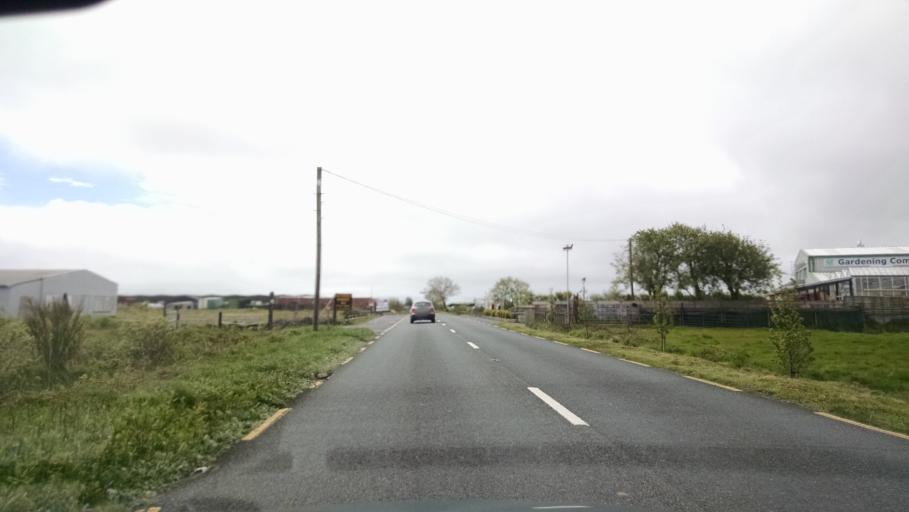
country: IE
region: Connaught
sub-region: County Galway
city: Gaillimh
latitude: 53.3361
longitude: -9.0199
